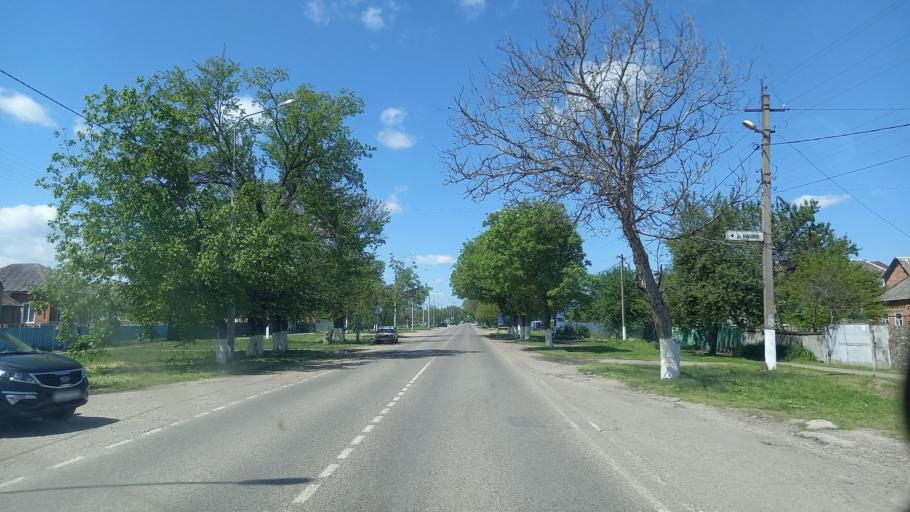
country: RU
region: Krasnodarskiy
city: Novoukrainskoye
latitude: 45.3804
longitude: 40.5149
